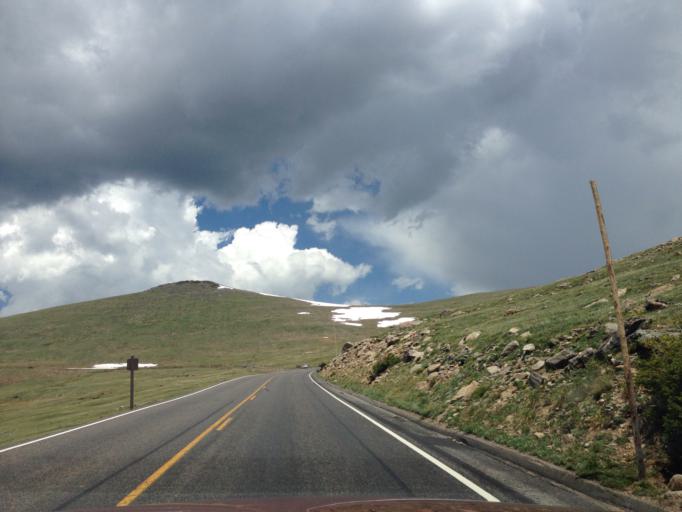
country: US
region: Colorado
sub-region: Larimer County
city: Estes Park
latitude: 40.3982
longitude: -105.7106
